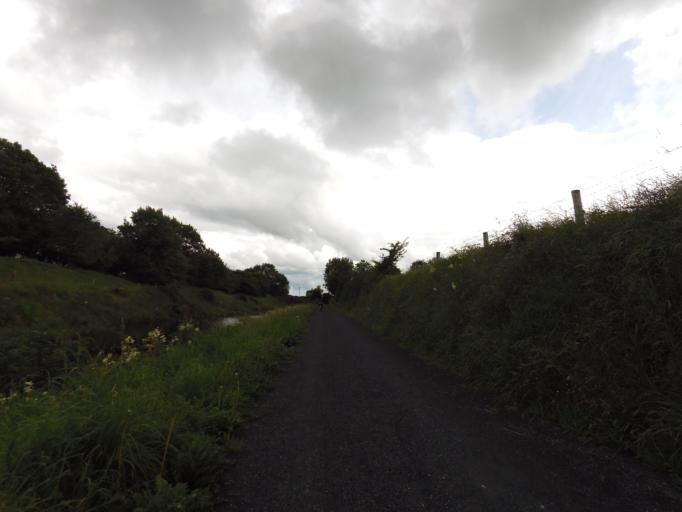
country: IE
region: Leinster
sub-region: An Iarmhi
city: An Muileann gCearr
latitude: 53.5258
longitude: -7.4472
